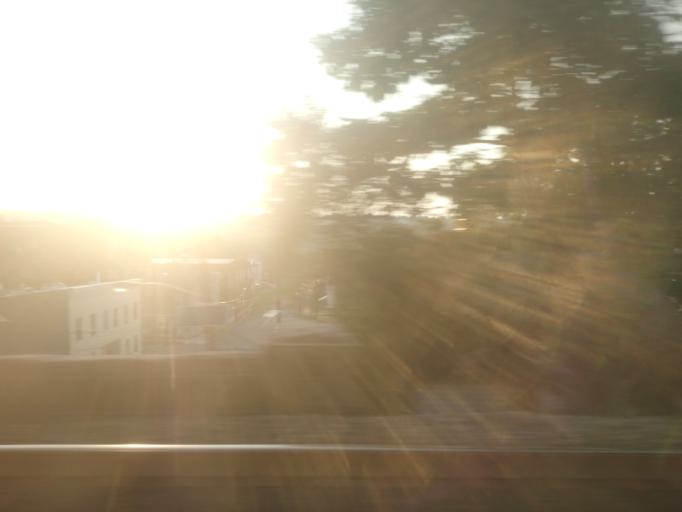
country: US
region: New Jersey
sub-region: Essex County
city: Orange
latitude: 40.7650
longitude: -74.2455
